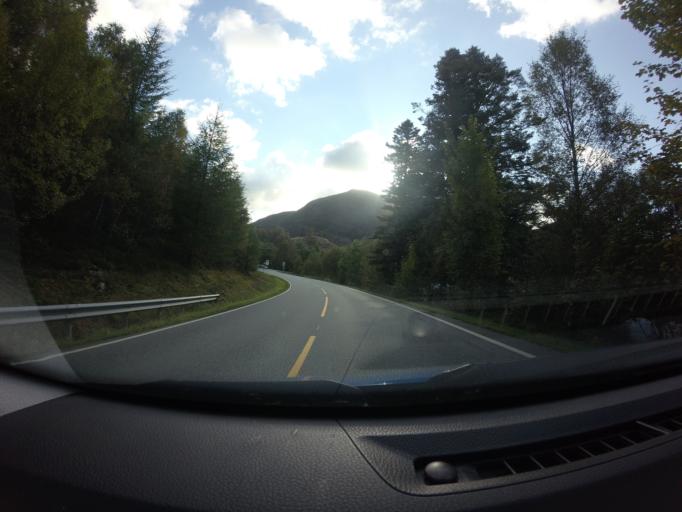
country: NO
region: Rogaland
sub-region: Forsand
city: Forsand
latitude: 58.8915
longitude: 6.0105
